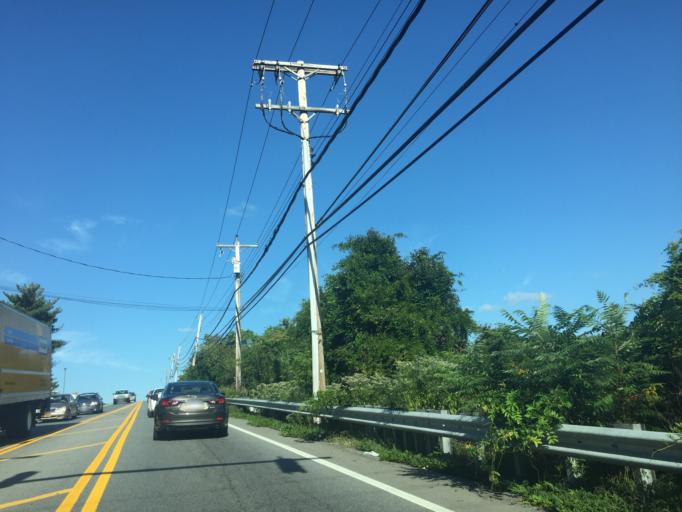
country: US
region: Maryland
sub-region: Baltimore County
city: Rossville
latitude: 39.3462
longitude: -76.4741
